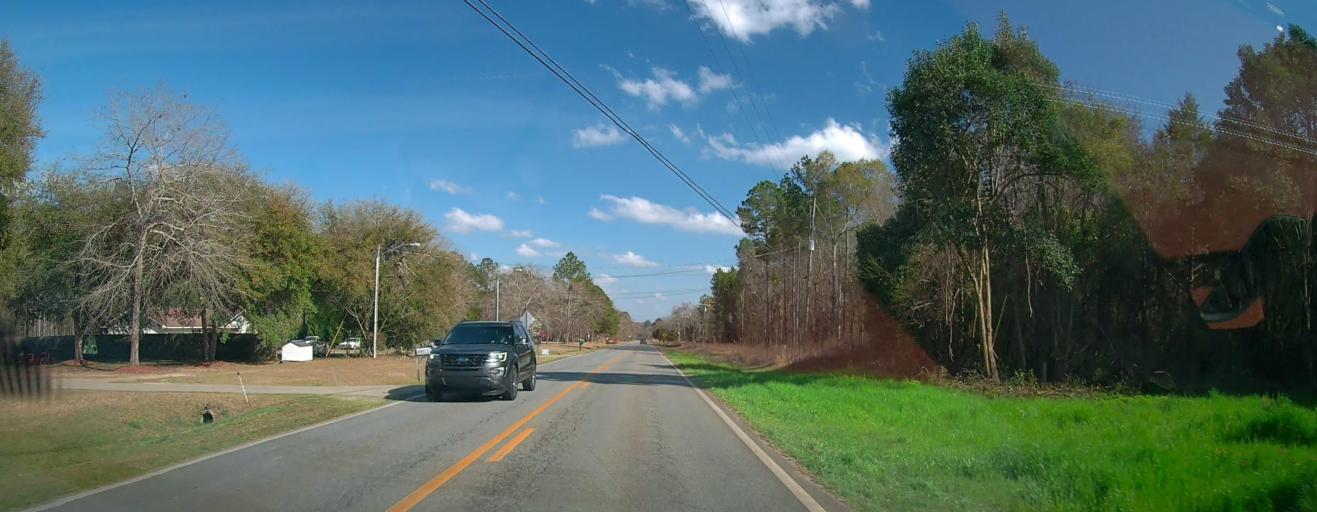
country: US
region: Georgia
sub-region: Laurens County
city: Dublin
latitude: 32.5596
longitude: -83.0073
